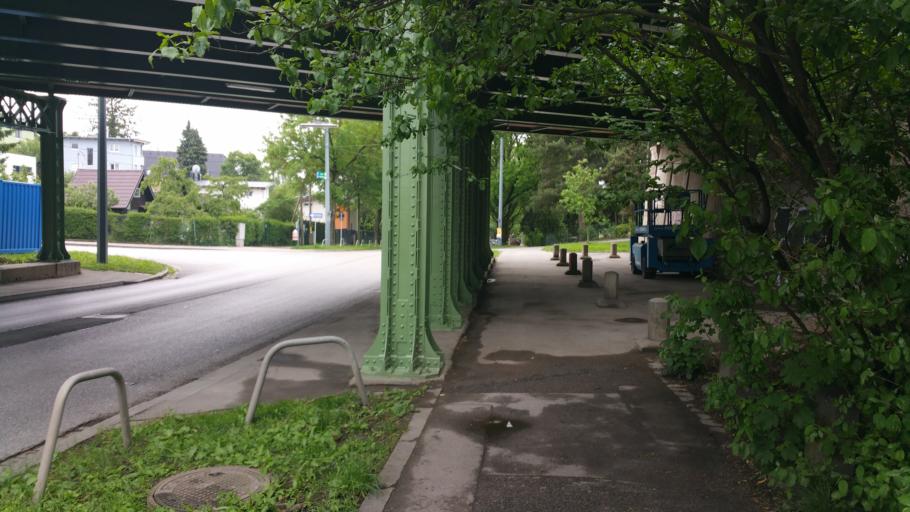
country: AT
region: Vienna
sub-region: Wien Stadt
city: Vienna
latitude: 48.2069
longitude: 16.2906
